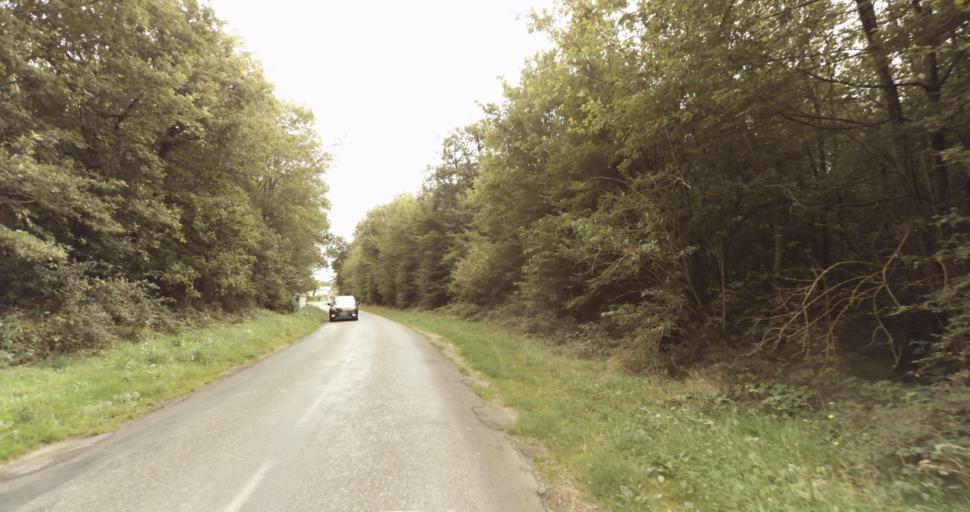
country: FR
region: Haute-Normandie
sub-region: Departement de l'Eure
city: Evreux
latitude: 48.9447
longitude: 1.1831
